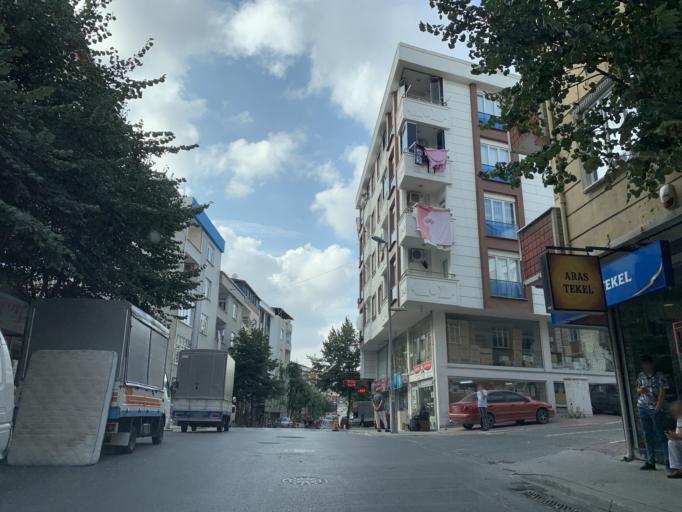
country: TR
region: Istanbul
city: Esenyurt
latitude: 41.0274
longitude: 28.6750
